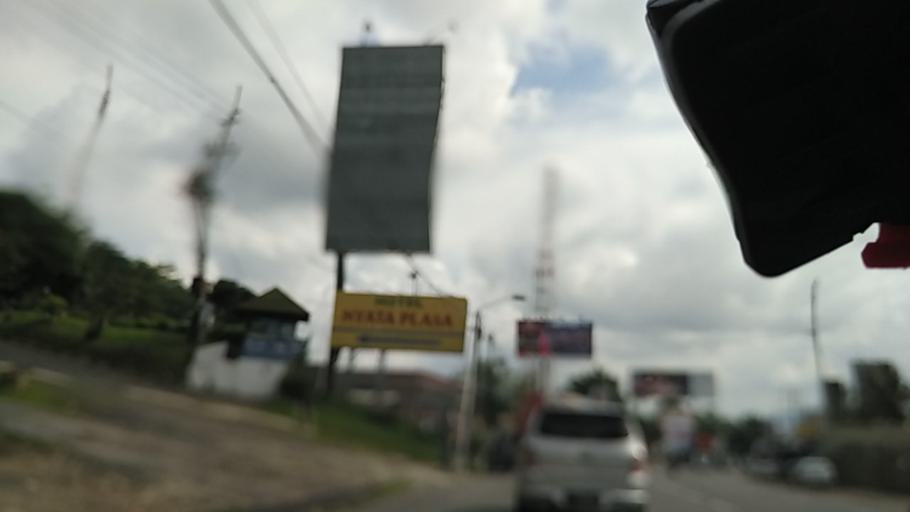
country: ID
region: Central Java
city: Semarang
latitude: -7.0421
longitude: 110.4222
